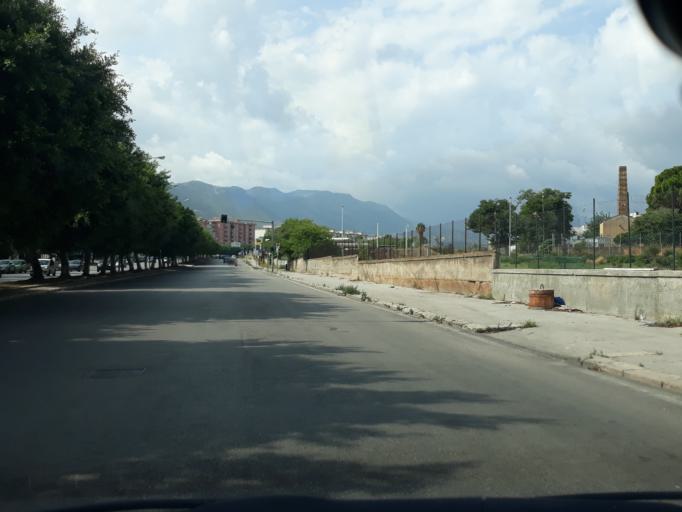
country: IT
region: Sicily
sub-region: Palermo
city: Palermo
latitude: 38.1017
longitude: 13.3479
